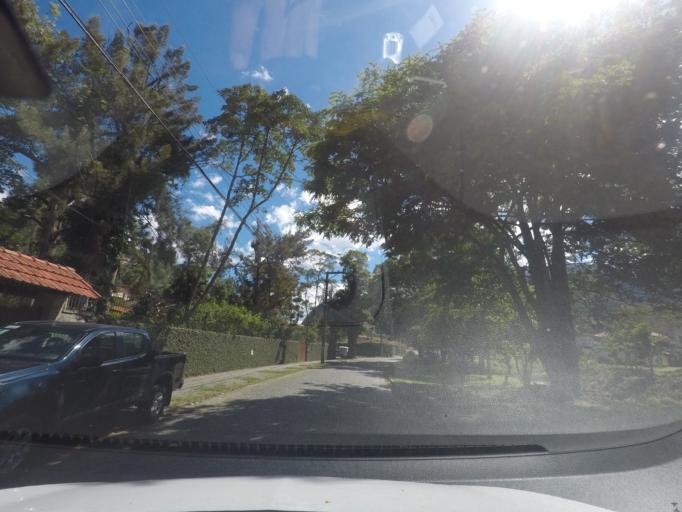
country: BR
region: Rio de Janeiro
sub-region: Teresopolis
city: Teresopolis
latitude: -22.4359
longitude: -42.9748
